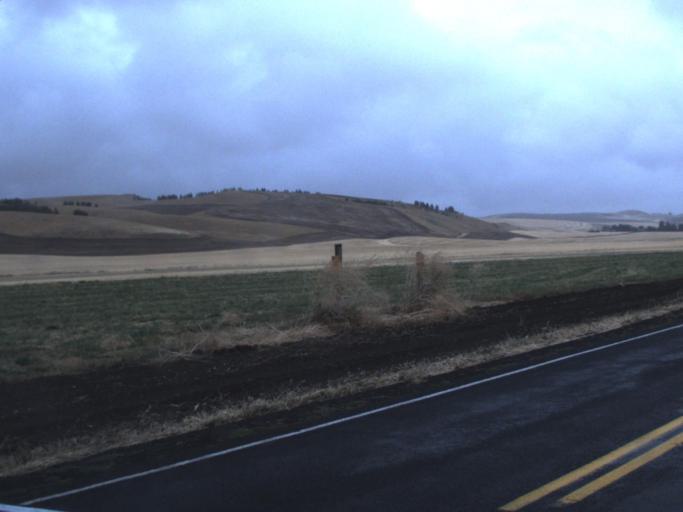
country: US
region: Washington
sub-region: Whitman County
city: Colfax
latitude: 47.0521
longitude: -117.5185
